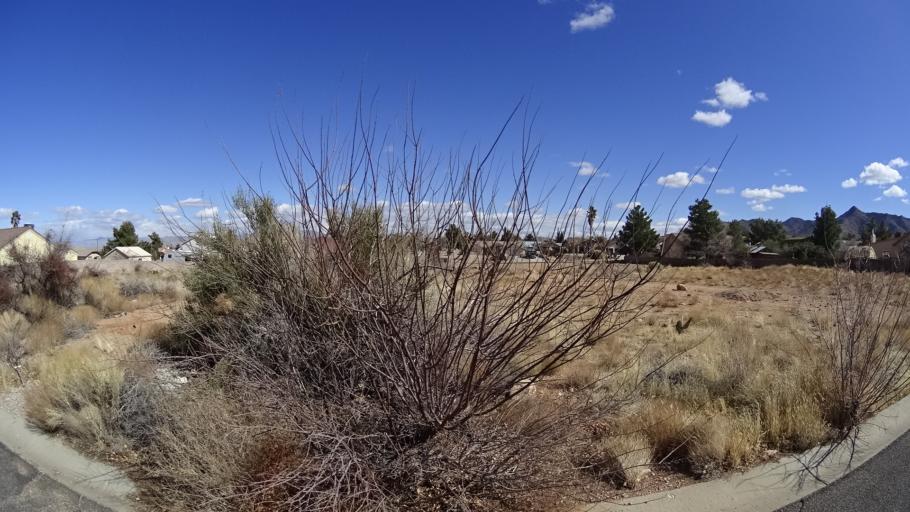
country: US
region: Arizona
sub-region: Mohave County
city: Kingman
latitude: 35.2015
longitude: -113.9718
